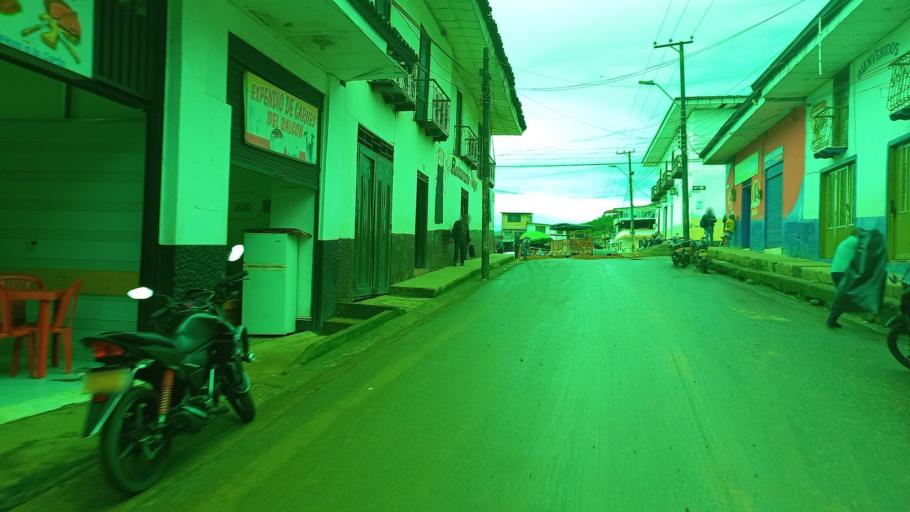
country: CO
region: Cauca
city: Balboa
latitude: 2.0413
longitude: -77.2162
